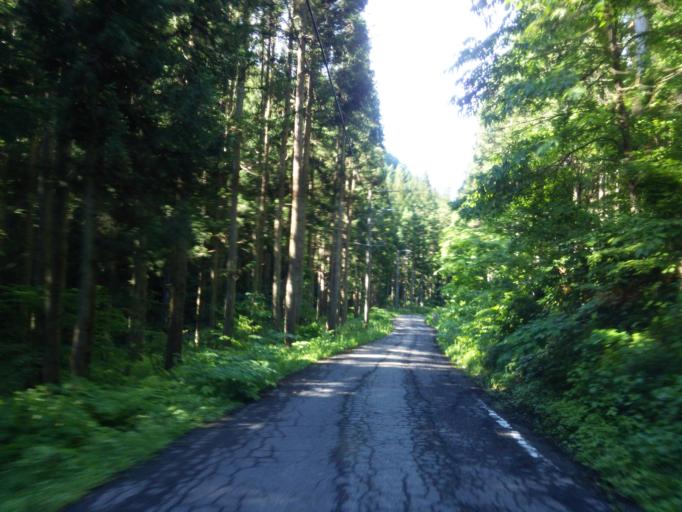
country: JP
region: Fukushima
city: Kitakata
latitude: 37.3802
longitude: 139.8101
